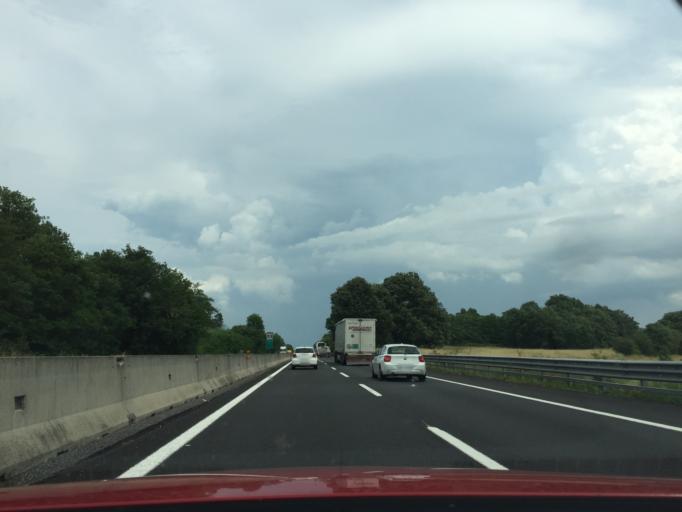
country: IT
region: Tuscany
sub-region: Provincia di Lucca
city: Altopascio
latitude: 43.8168
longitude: 10.6467
